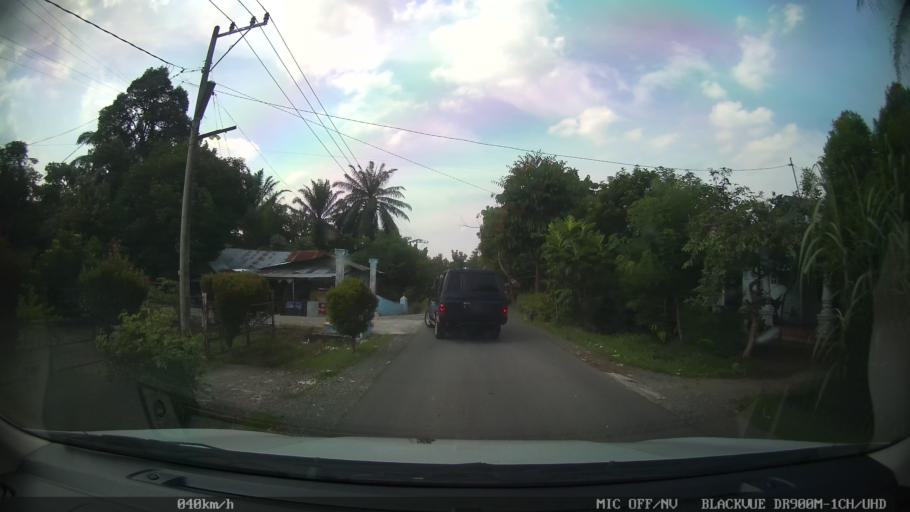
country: ID
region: North Sumatra
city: Binjai
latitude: 3.6363
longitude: 98.5174
